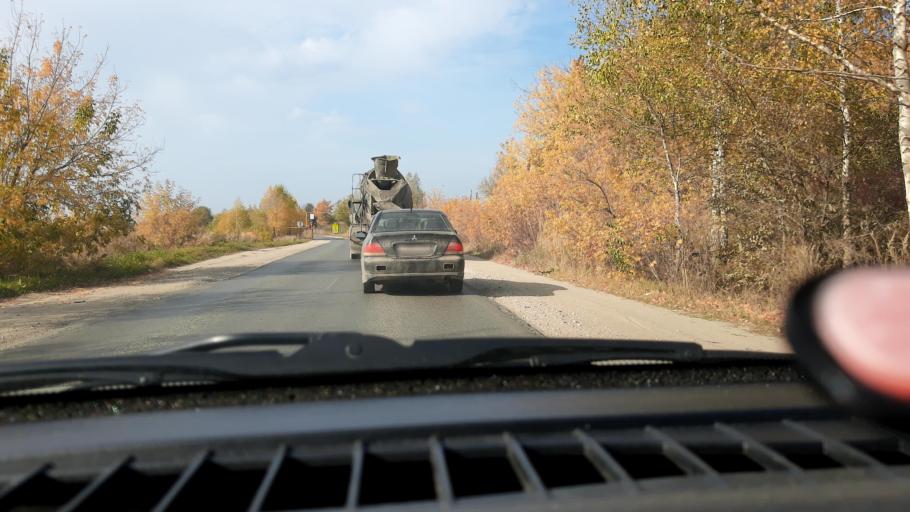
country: RU
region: Nizjnij Novgorod
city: Neklyudovo
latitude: 56.4198
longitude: 43.9641
